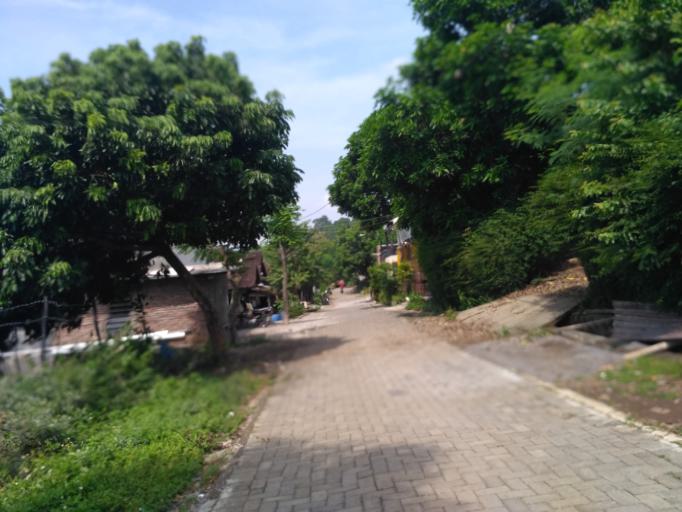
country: ID
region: Central Java
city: Semarang
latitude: -7.0442
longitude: 110.4417
